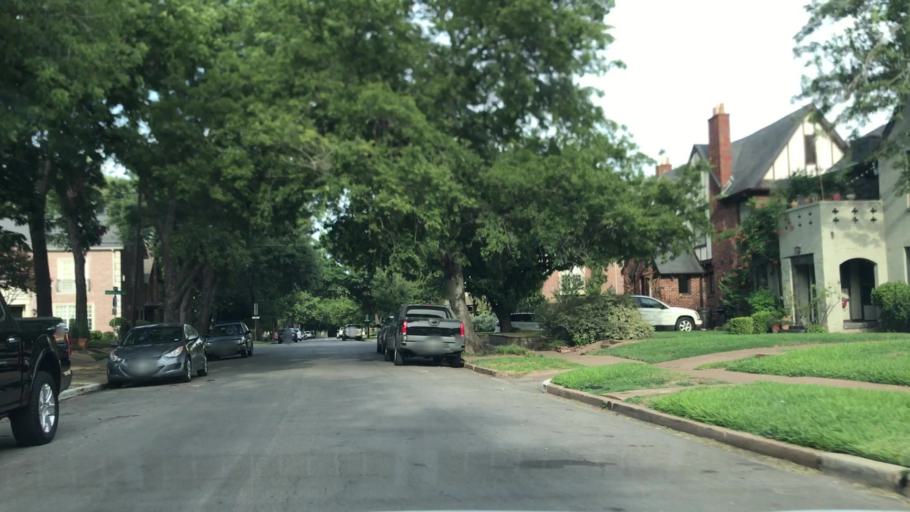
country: US
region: Texas
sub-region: Dallas County
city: Highland Park
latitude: 32.8217
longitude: -96.8052
